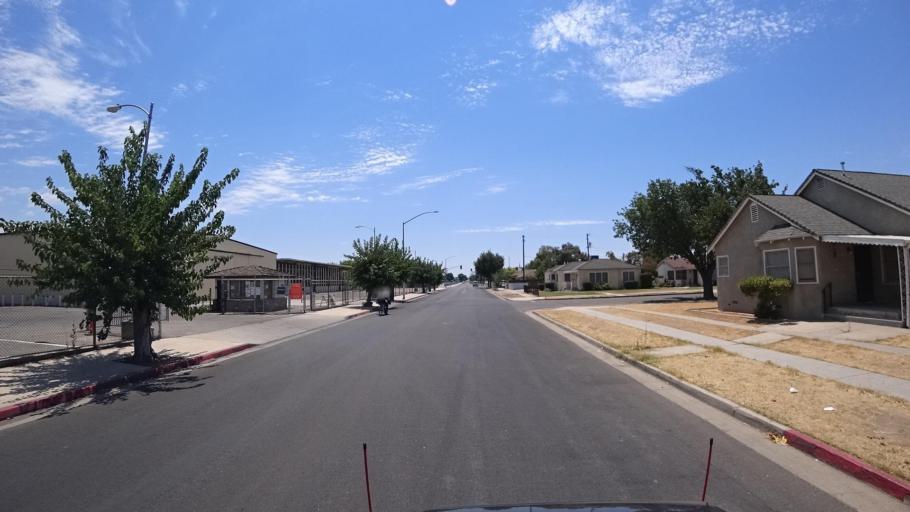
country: US
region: California
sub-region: Fresno County
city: Fresno
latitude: 36.7299
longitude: -119.7512
